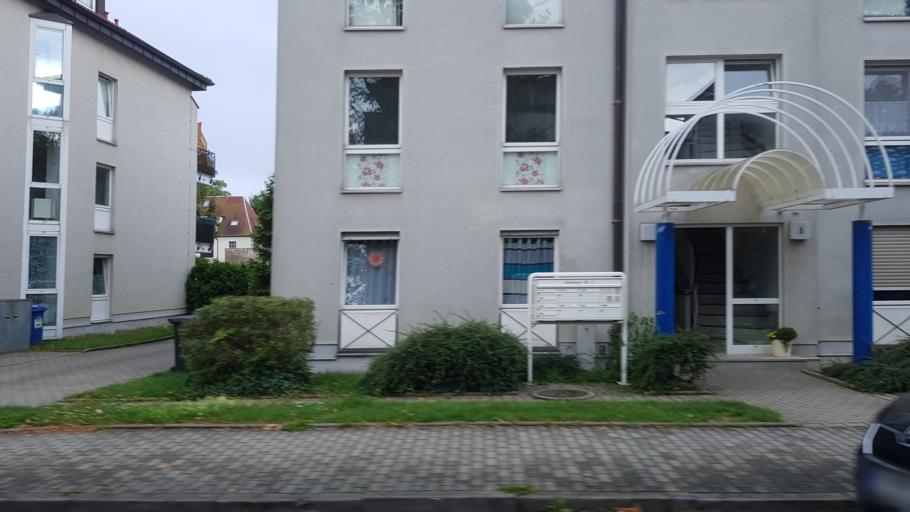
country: DE
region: Saxony
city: Heidenau
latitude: 51.0280
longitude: 13.8331
